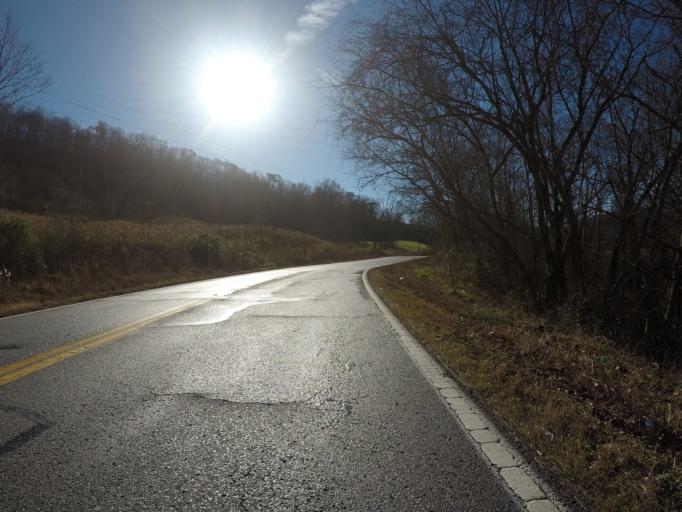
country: US
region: West Virginia
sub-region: Cabell County
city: Huntington
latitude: 38.4753
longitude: -82.4430
